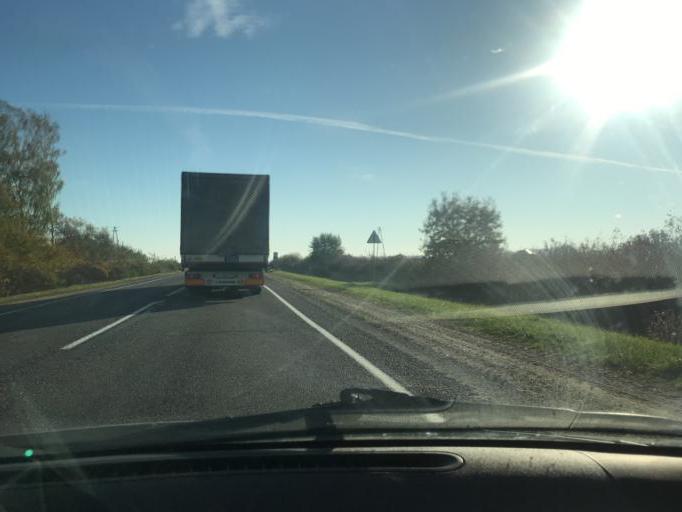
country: BY
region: Brest
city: Ivanava
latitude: 52.1473
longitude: 25.4399
